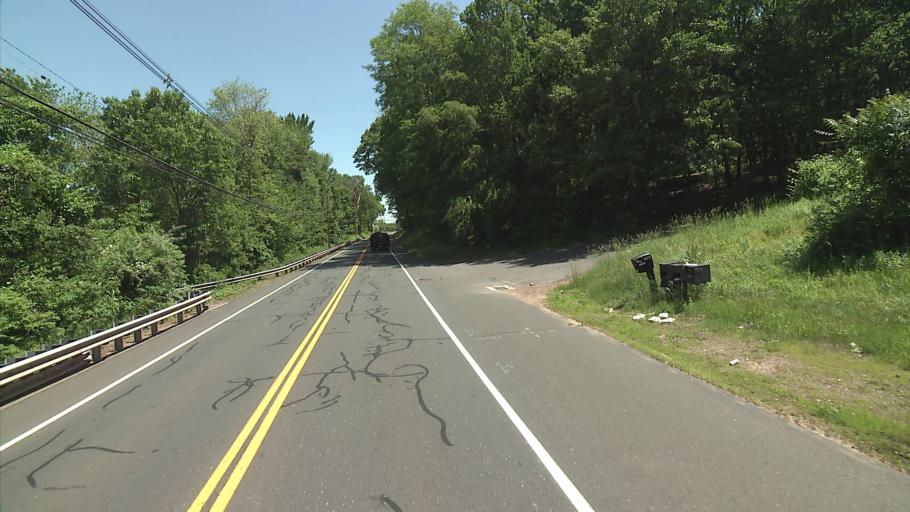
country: US
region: Connecticut
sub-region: Tolland County
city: Rockville
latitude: 41.8512
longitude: -72.4475
